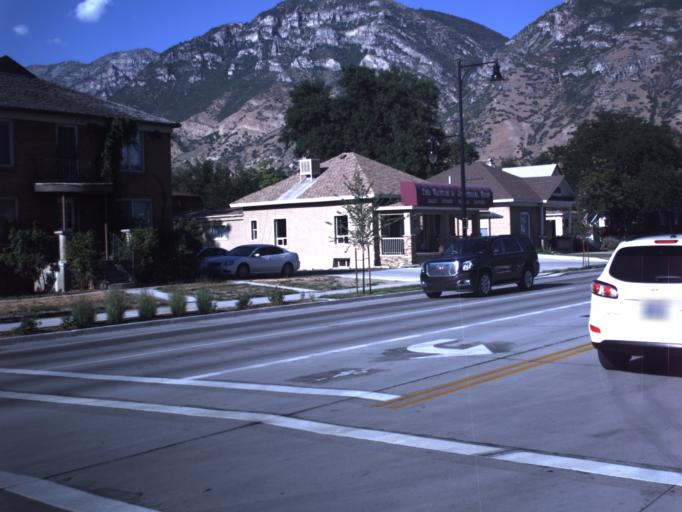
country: US
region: Utah
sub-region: Utah County
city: Provo
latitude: 40.2296
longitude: -111.6525
